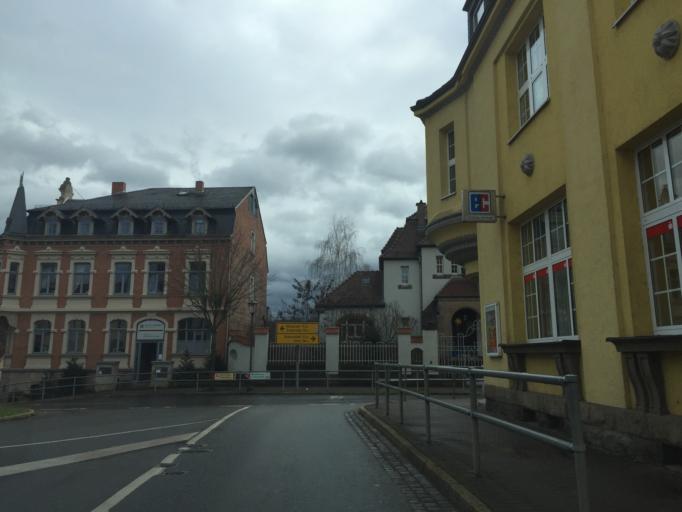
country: DE
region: Thuringia
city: Kahla
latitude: 50.8013
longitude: 11.5865
